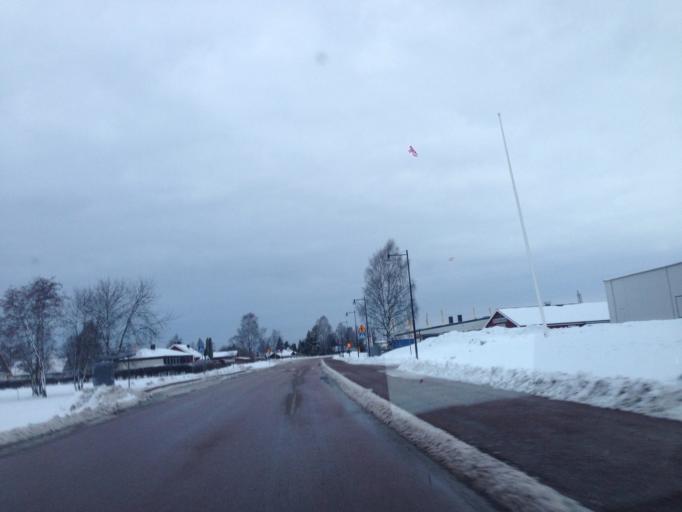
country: SE
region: Dalarna
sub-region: Mora Kommun
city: Mora
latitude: 61.0058
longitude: 14.5939
